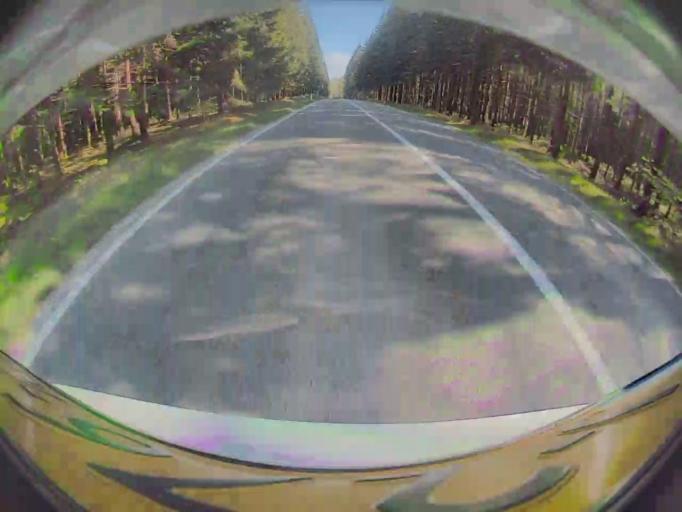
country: BE
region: Wallonia
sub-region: Province du Luxembourg
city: Libin
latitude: 50.0172
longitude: 5.2043
